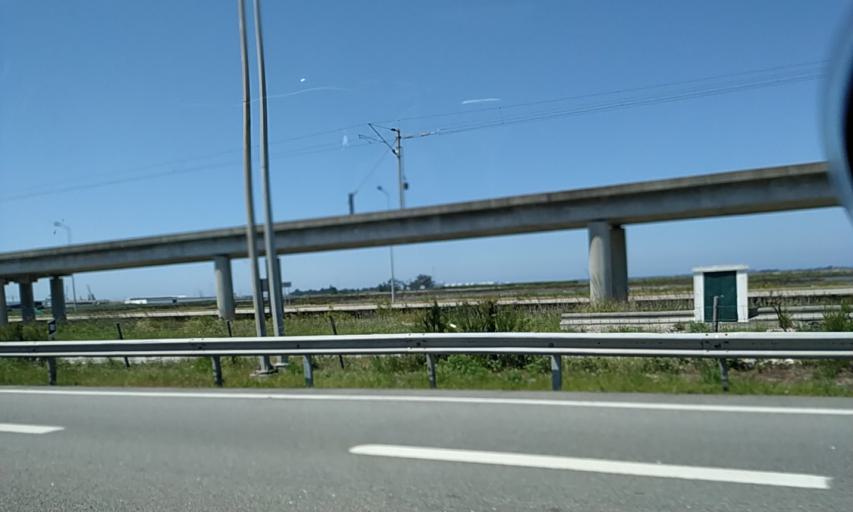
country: PT
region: Aveiro
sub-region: Aveiro
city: Aveiro
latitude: 40.6401
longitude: -8.6636
